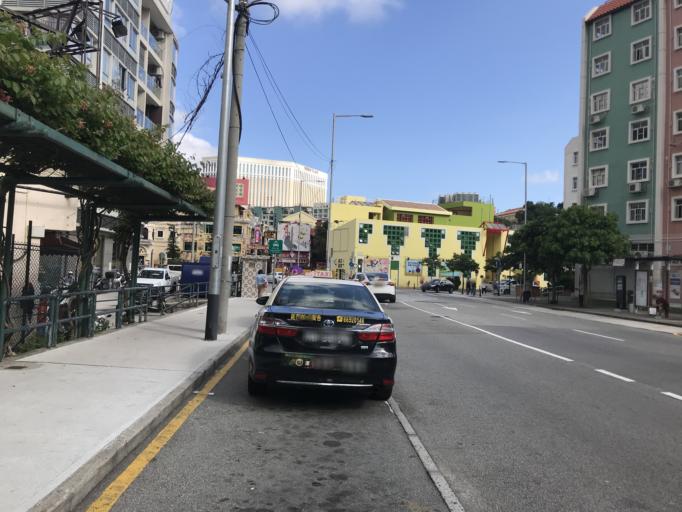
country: MO
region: Macau
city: Macau
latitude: 22.1548
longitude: 113.5561
